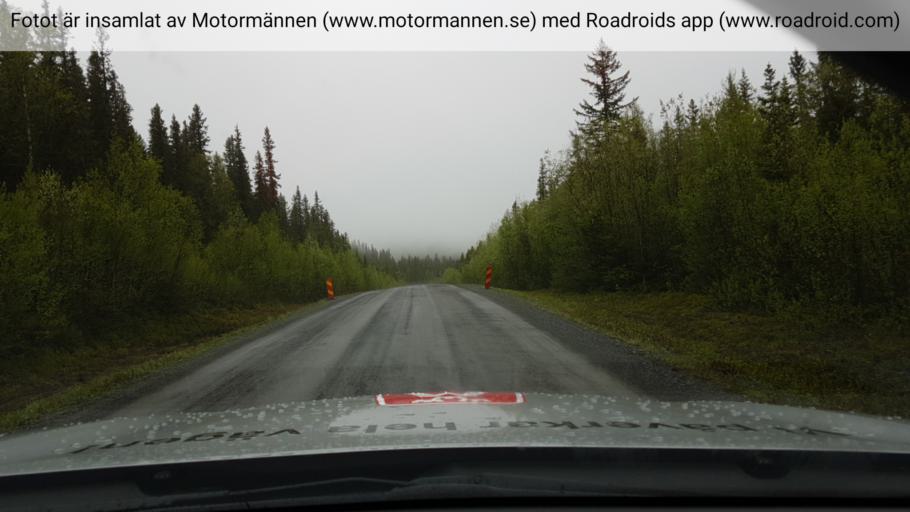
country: SE
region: Jaemtland
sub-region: Krokoms Kommun
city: Valla
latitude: 63.1033
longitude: 13.8717
